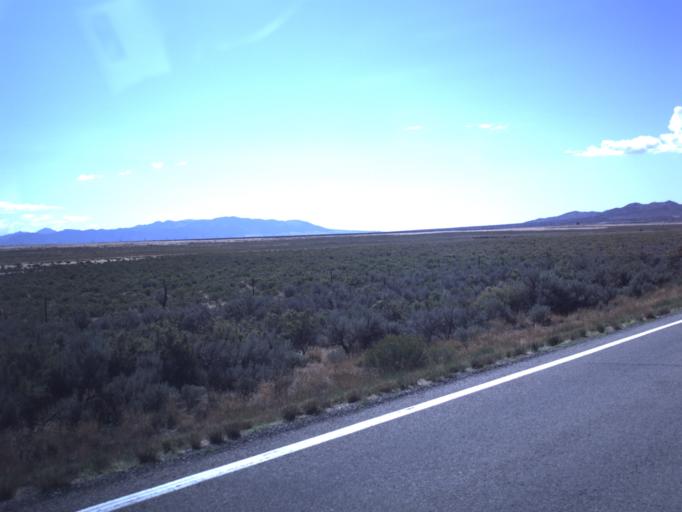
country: US
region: Utah
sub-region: Tooele County
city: Tooele
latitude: 40.2229
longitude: -112.4049
